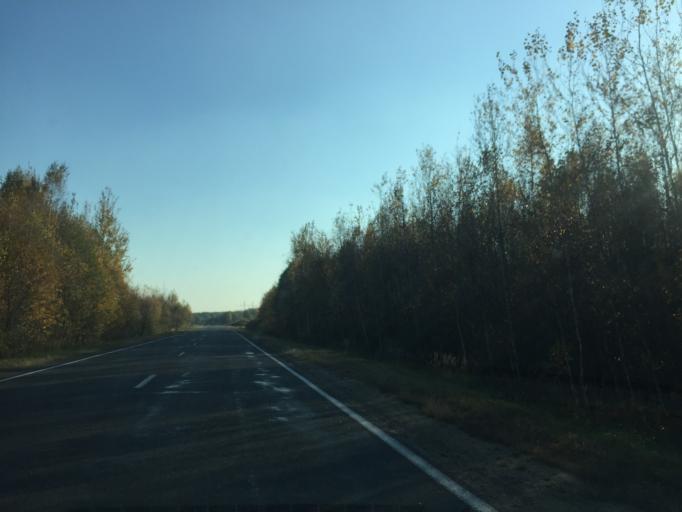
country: BY
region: Gomel
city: Dobrush
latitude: 52.3487
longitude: 31.2294
